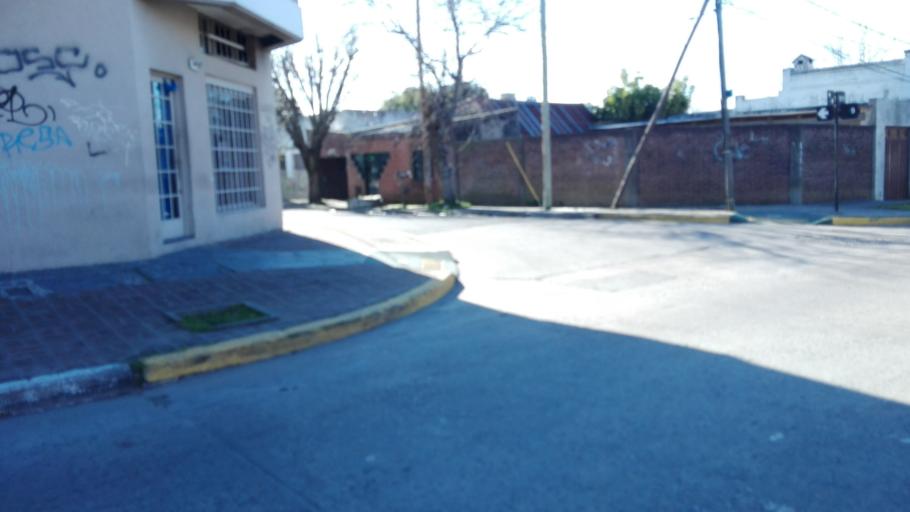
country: AR
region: Buenos Aires
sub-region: Partido de La Plata
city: La Plata
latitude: -34.8845
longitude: -57.9944
